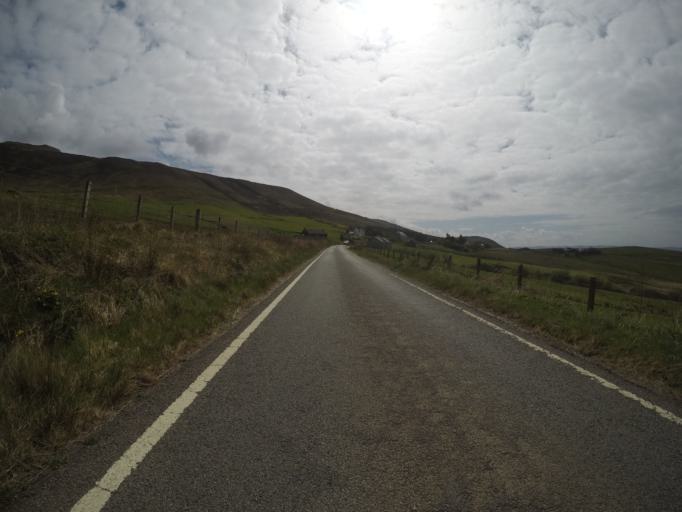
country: GB
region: Scotland
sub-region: Highland
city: Portree
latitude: 57.6143
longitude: -6.3710
